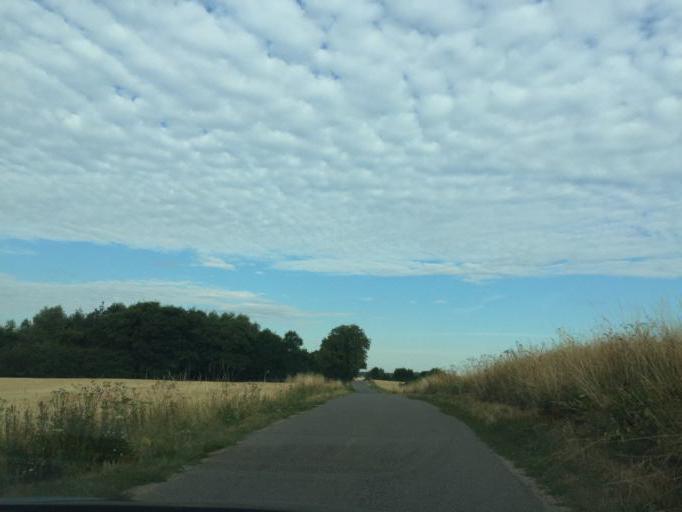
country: DK
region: South Denmark
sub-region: Assens Kommune
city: Assens
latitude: 55.3190
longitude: 9.9636
